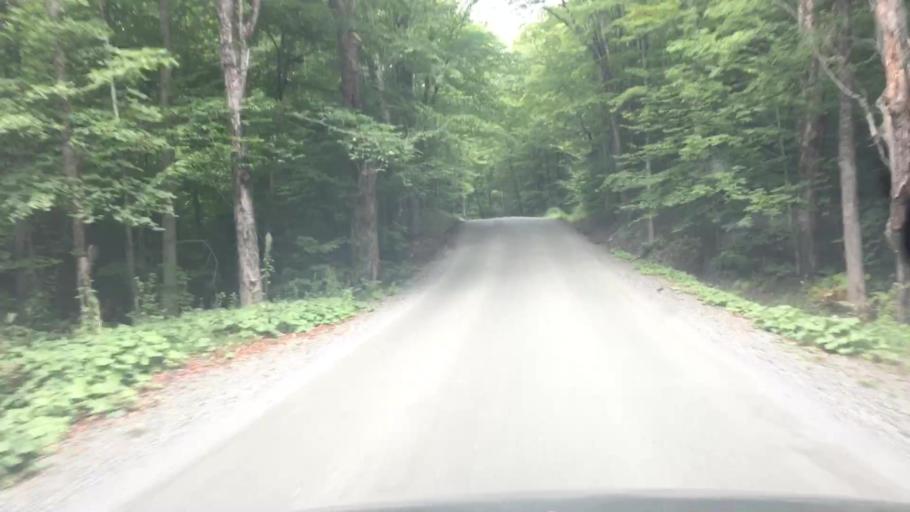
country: US
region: Vermont
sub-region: Windham County
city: Dover
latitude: 42.8211
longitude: -72.7730
